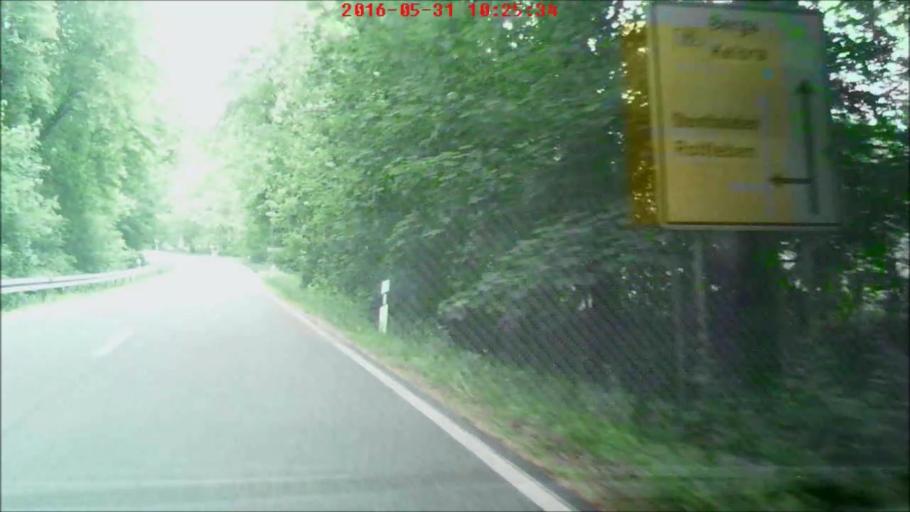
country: DE
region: Thuringia
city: Bad Frankenhausen
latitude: 51.3909
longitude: 11.0787
